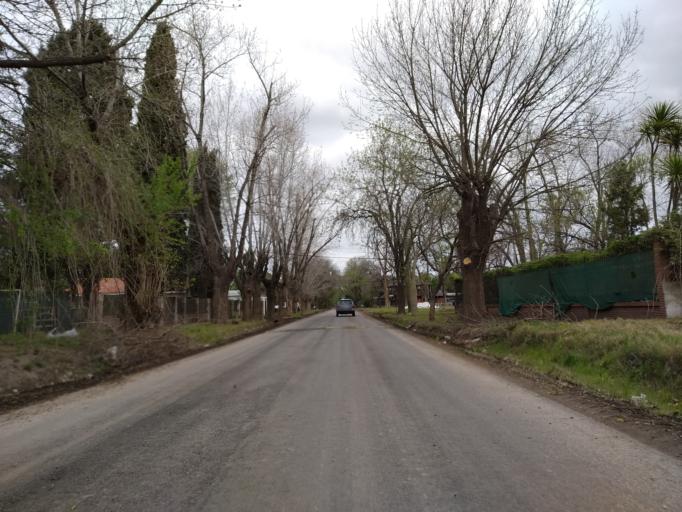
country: AR
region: Santa Fe
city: Funes
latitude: -32.9181
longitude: -60.8513
